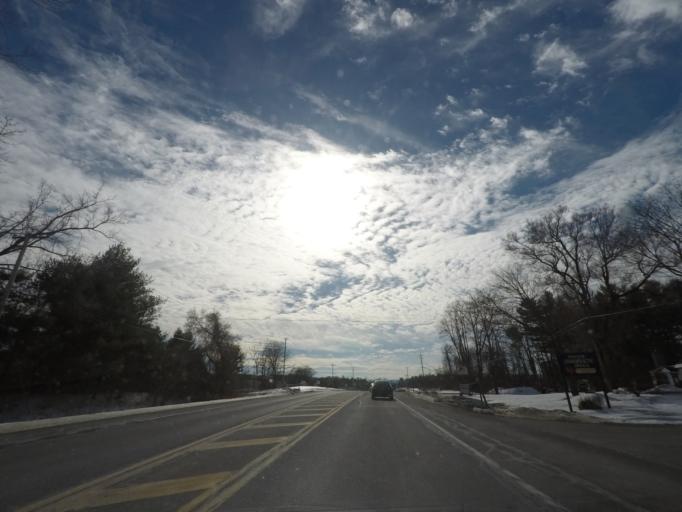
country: US
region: New York
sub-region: Albany County
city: Westmere
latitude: 42.7002
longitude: -73.8855
